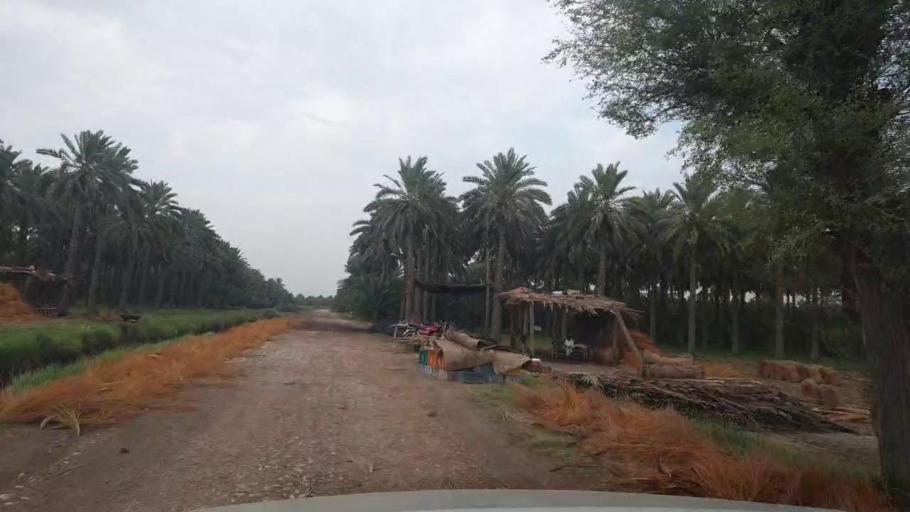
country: PK
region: Sindh
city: Sukkur
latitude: 27.6112
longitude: 68.8357
